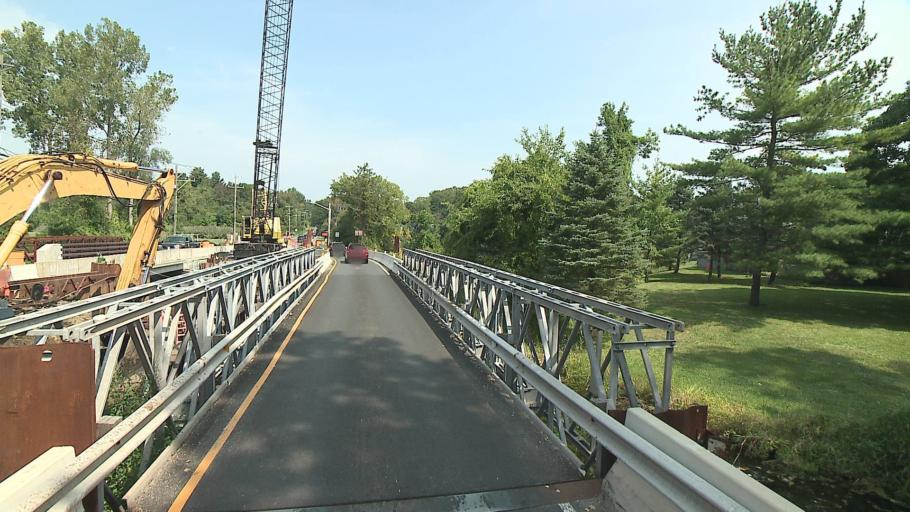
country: US
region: Connecticut
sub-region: Fairfield County
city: Ridgefield
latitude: 41.2976
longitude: -73.4923
